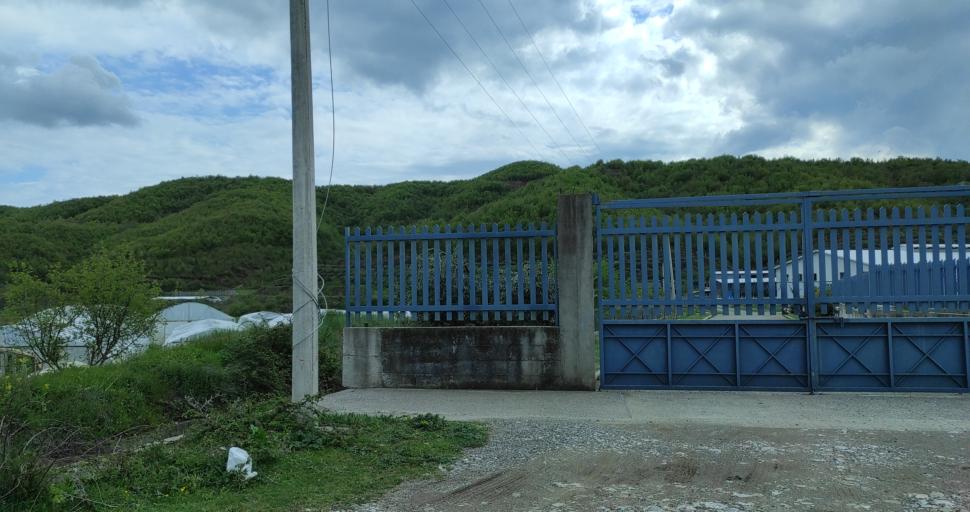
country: AL
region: Shkoder
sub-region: Rrethi i Shkodres
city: Dajc
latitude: 42.0364
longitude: 19.4014
